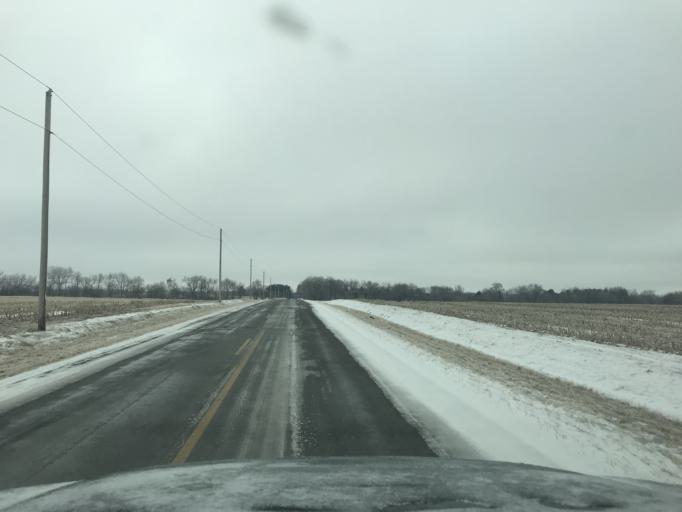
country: US
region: Wisconsin
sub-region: Dane County
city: Cottage Grove
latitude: 43.1006
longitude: -89.2296
